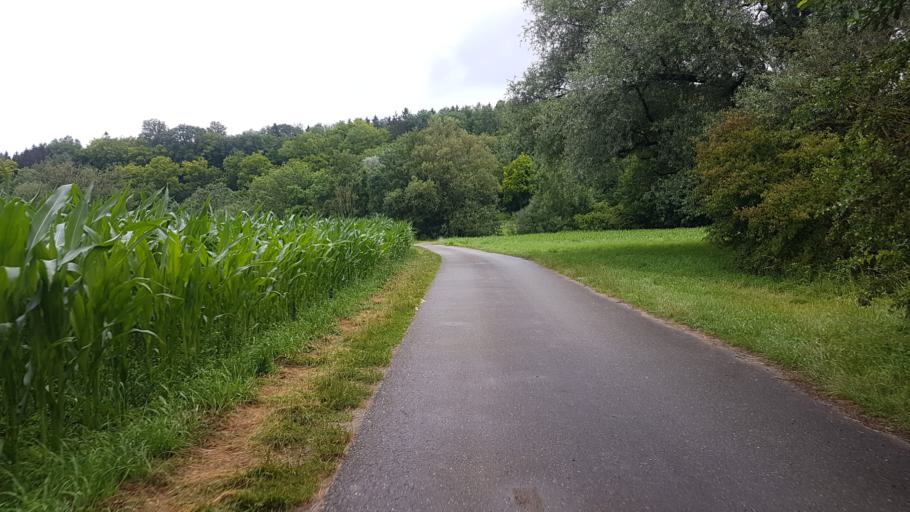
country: DE
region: Baden-Wuerttemberg
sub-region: Tuebingen Region
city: Rottenacker
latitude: 48.2409
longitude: 9.7080
